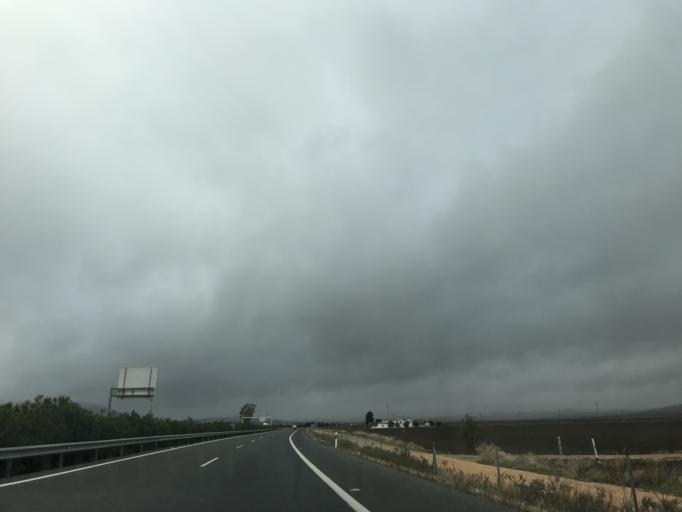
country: ES
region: Andalusia
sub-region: Provincia de Malaga
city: Mollina
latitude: 37.0764
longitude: -4.6093
